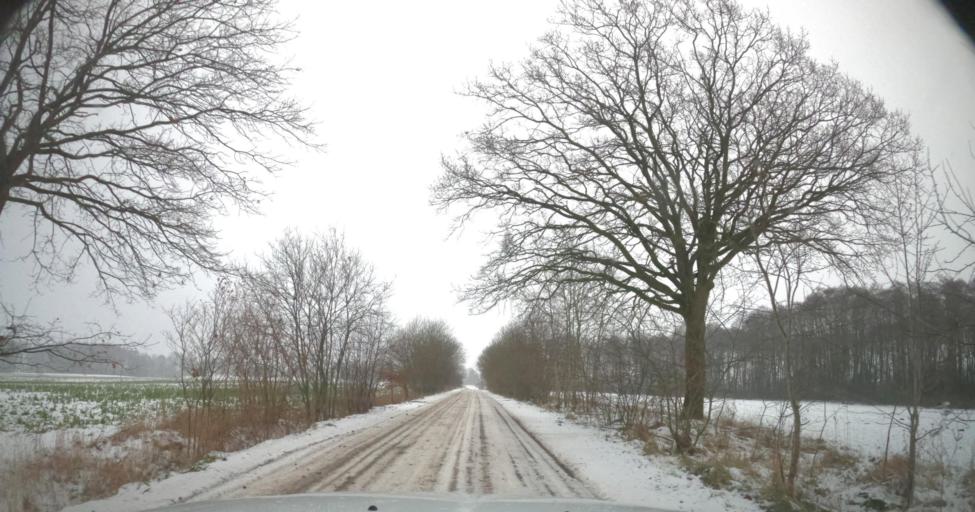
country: PL
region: West Pomeranian Voivodeship
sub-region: Powiat gryficki
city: Brojce
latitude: 53.9045
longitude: 15.3347
